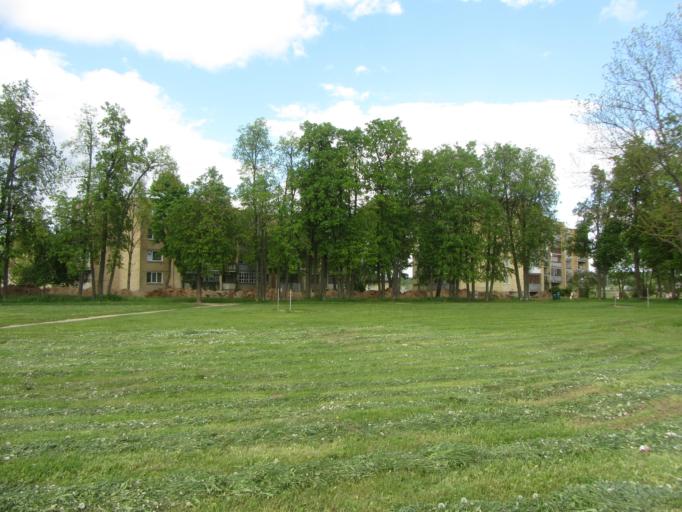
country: LT
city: Sirvintos
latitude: 55.0475
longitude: 24.9565
